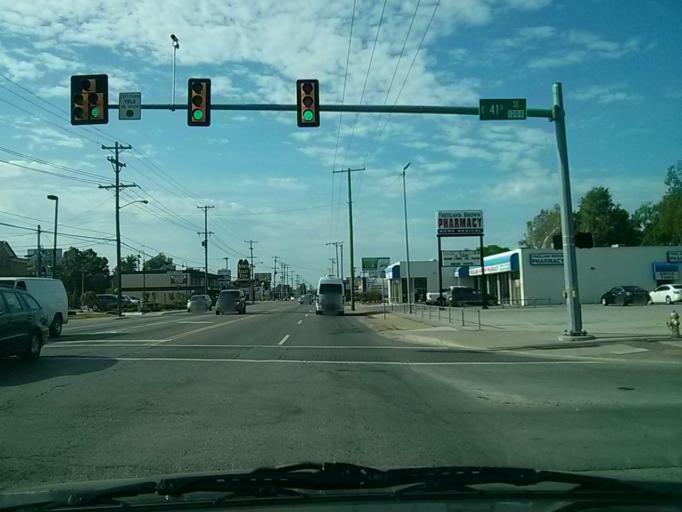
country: US
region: Oklahoma
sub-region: Tulsa County
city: Tulsa
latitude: 36.1043
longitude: -95.9758
